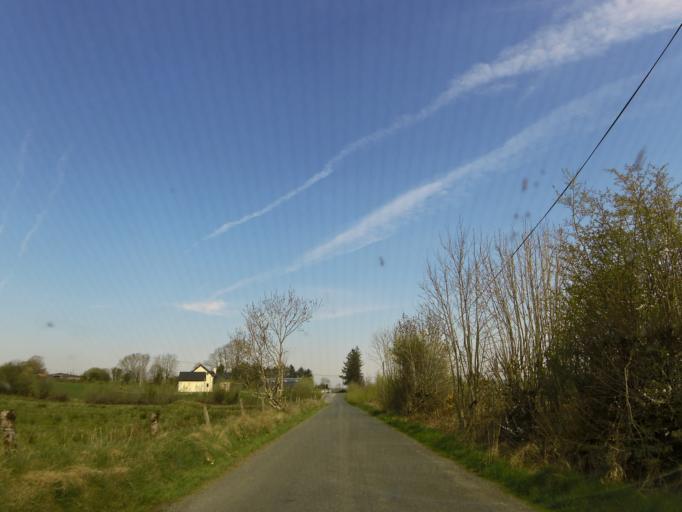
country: IE
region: Connaught
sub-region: Maigh Eo
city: Kiltamagh
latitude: 53.8017
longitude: -8.9706
